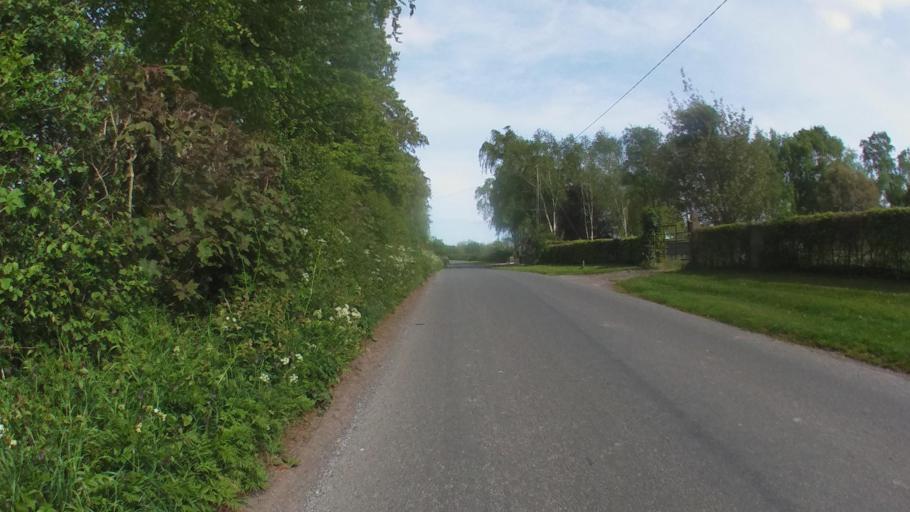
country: IE
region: Leinster
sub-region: County Carlow
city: Carlow
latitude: 52.8314
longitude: -6.9654
